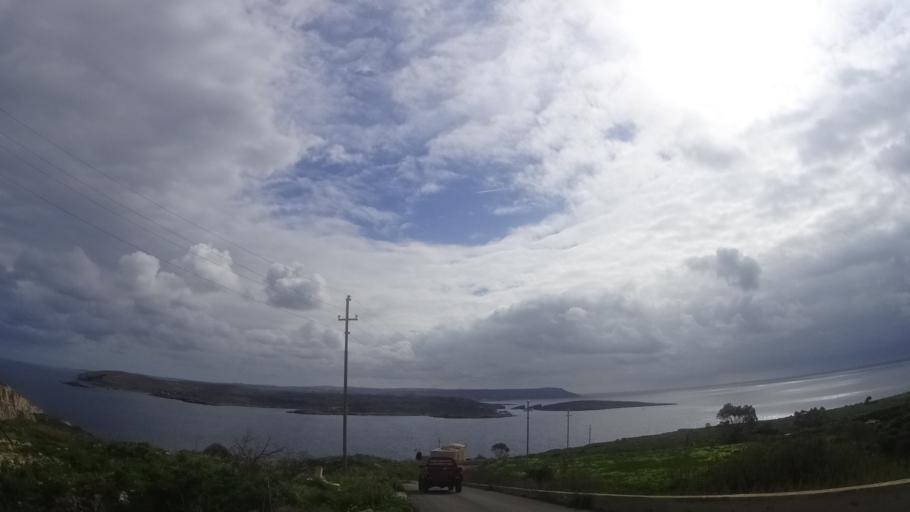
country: MT
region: Il-Qala
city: Qala
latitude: 36.0306
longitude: 14.3210
